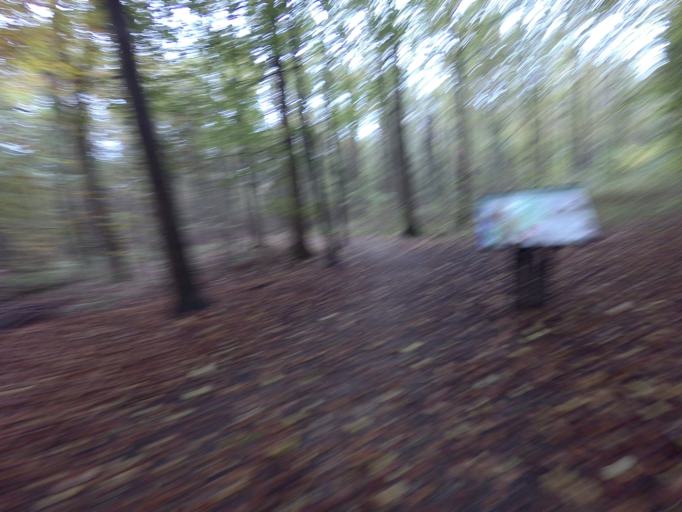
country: NL
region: Friesland
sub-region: Gemeente Lemsterland
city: Echtenerbrug
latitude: 52.7837
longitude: 5.8395
